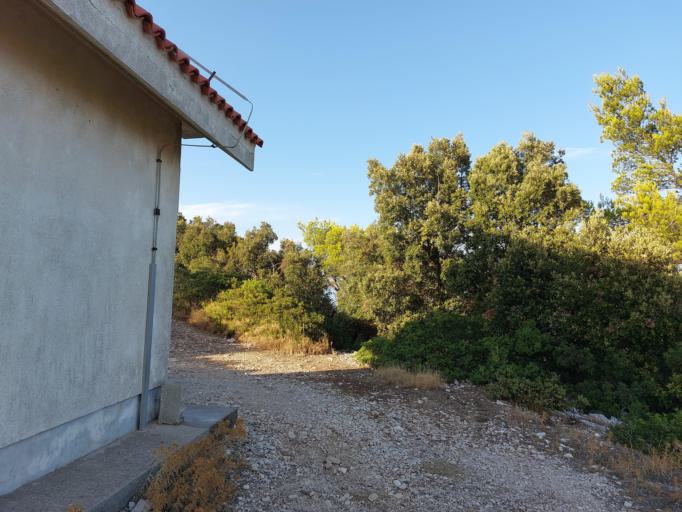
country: HR
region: Dubrovacko-Neretvanska
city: Smokvica
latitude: 42.7514
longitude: 16.8607
